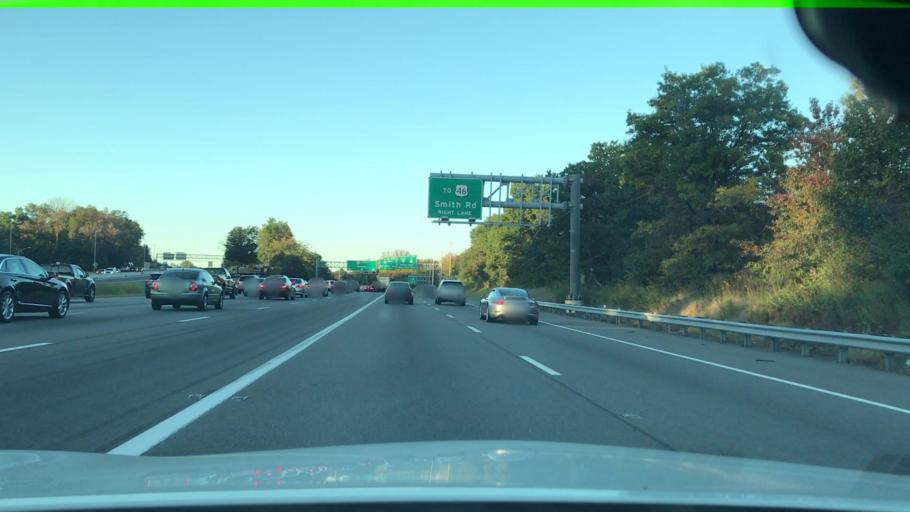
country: US
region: New Jersey
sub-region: Morris County
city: Parsippany
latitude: 40.8595
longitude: -74.4194
